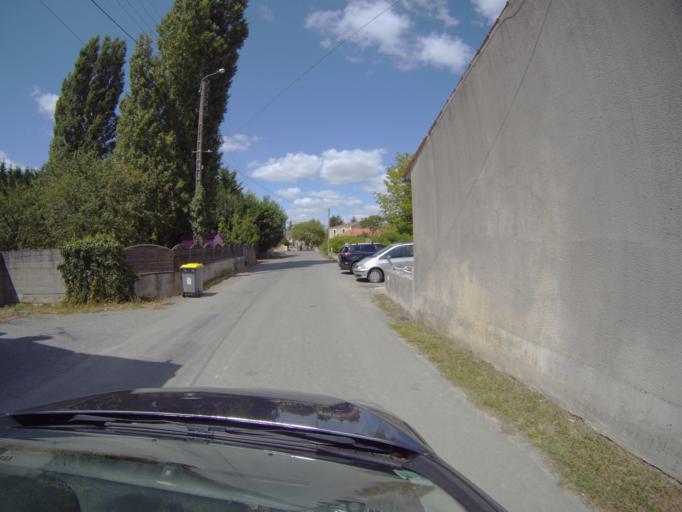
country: FR
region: Poitou-Charentes
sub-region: Departement des Deux-Sevres
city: Saint-Hilaire-la-Palud
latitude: 46.2779
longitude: -0.6521
